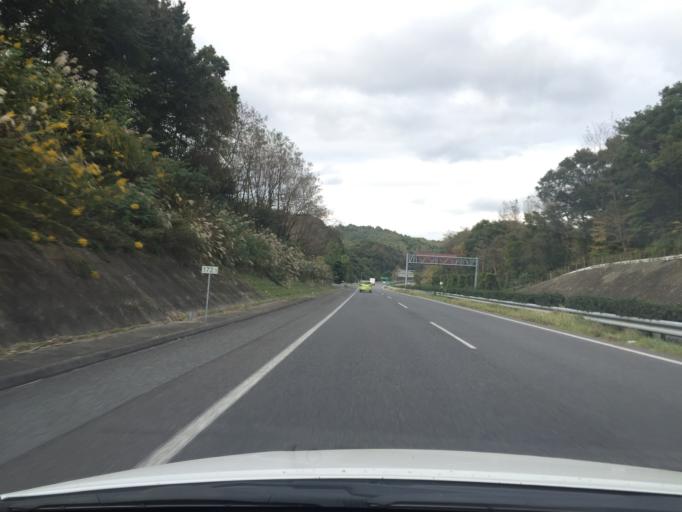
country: JP
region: Fukushima
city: Iwaki
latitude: 37.0447
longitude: 140.8207
